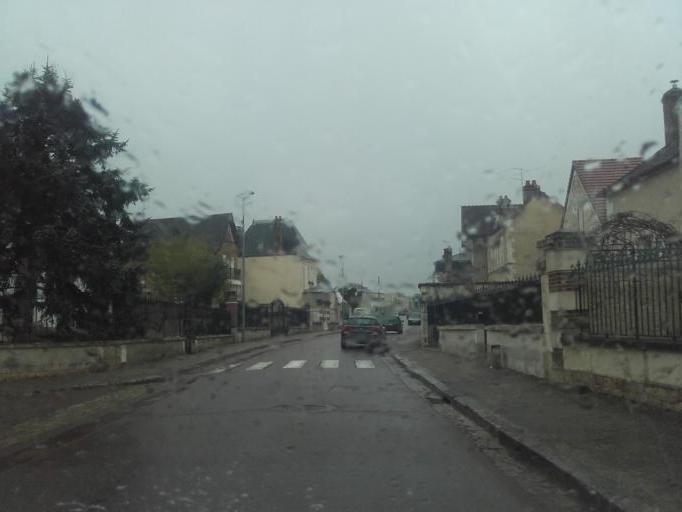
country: FR
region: Bourgogne
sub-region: Departement de l'Yonne
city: Chablis
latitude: 47.8142
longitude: 3.7974
